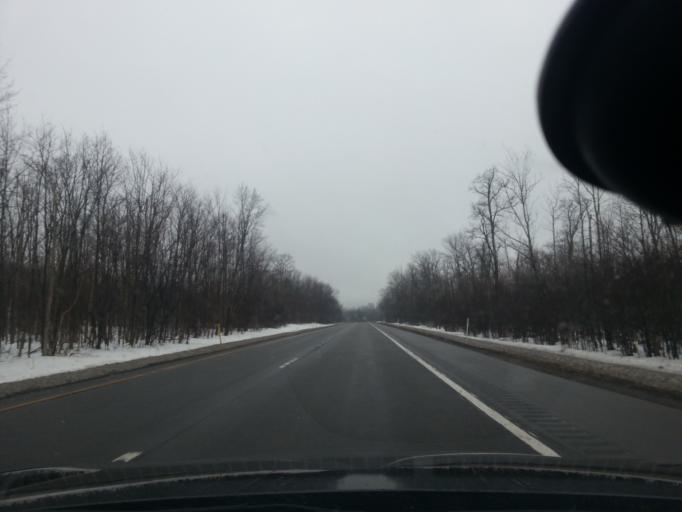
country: US
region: New York
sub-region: Jefferson County
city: Adams
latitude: 43.7479
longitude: -76.0671
